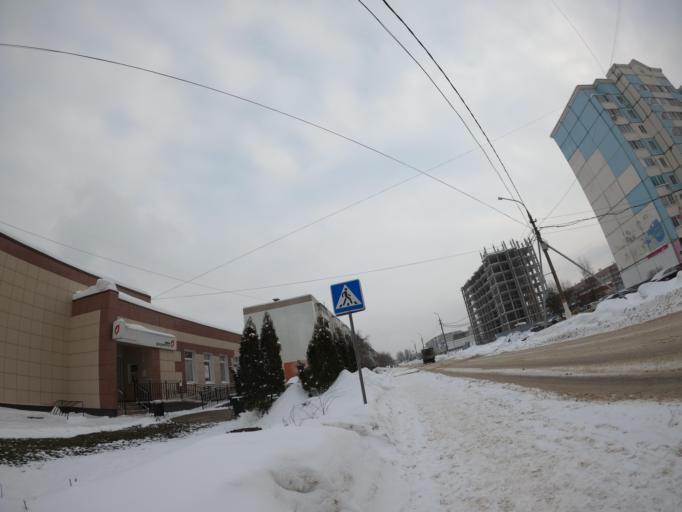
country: RU
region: Moskovskaya
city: Elektrogorsk
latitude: 55.8839
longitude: 38.7756
